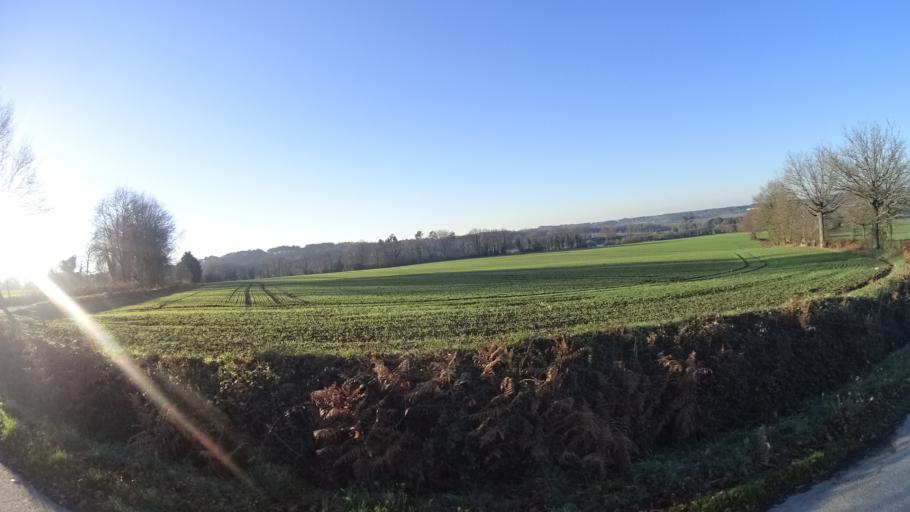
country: FR
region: Brittany
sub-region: Departement du Morbihan
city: Allaire
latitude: 47.6637
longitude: -2.1654
